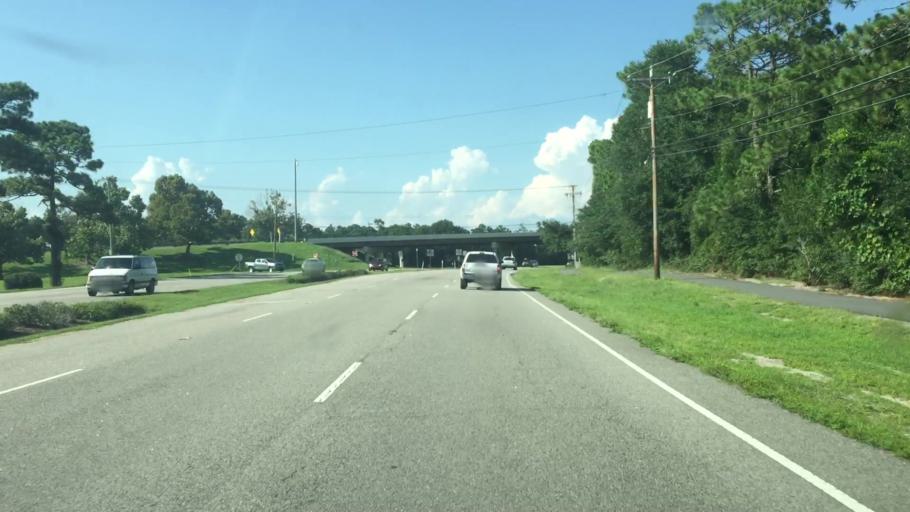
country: US
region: South Carolina
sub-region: Horry County
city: Myrtle Beach
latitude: 33.7655
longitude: -78.8056
